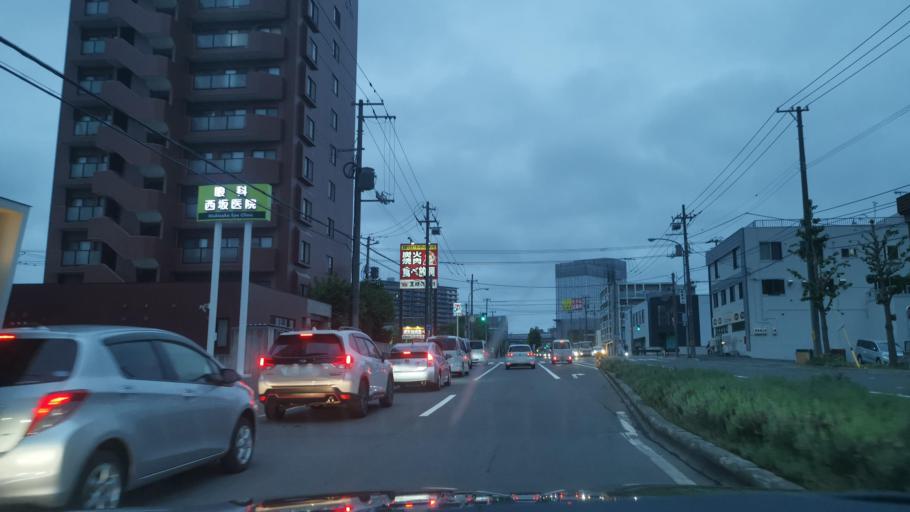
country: JP
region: Hokkaido
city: Sapporo
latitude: 43.0937
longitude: 141.2708
